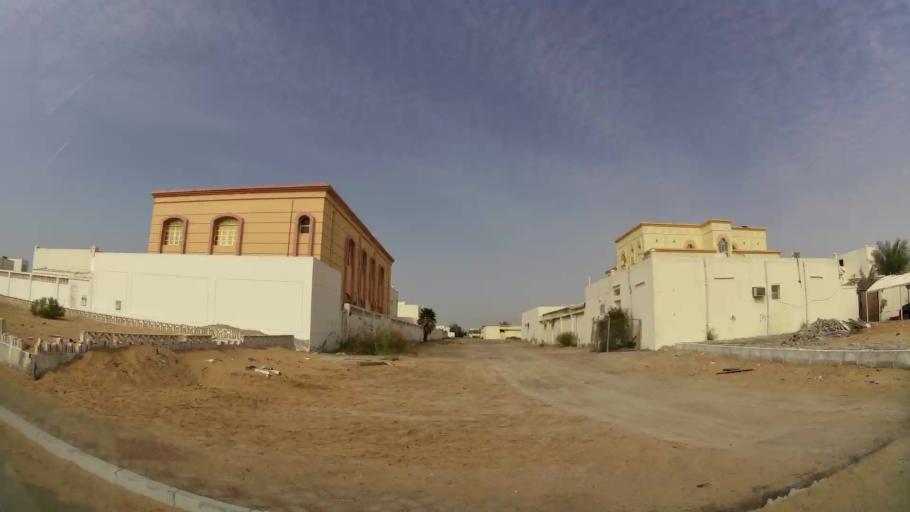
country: AE
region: Abu Dhabi
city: Abu Dhabi
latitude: 24.5941
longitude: 54.6969
